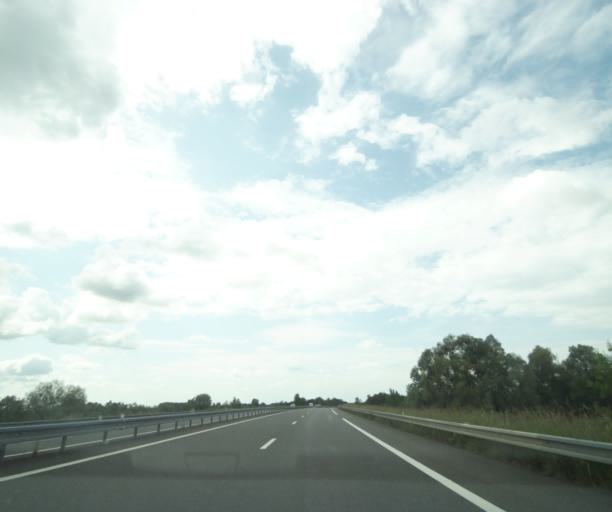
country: FR
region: Pays de la Loire
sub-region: Departement de Maine-et-Loire
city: Vivy
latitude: 47.3416
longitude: -0.0621
